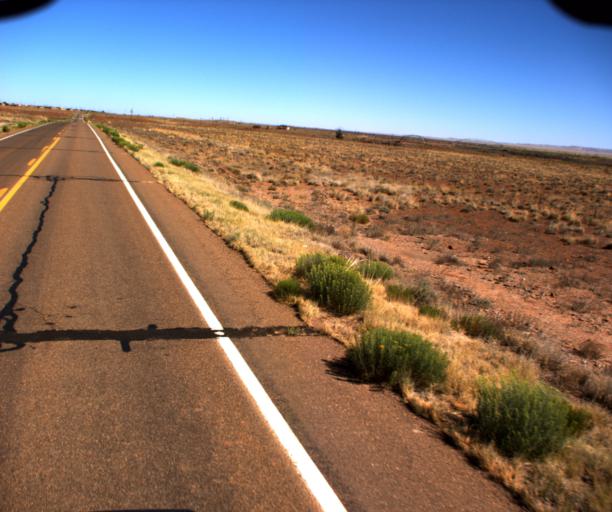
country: US
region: Arizona
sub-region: Coconino County
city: LeChee
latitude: 35.2909
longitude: -110.9868
